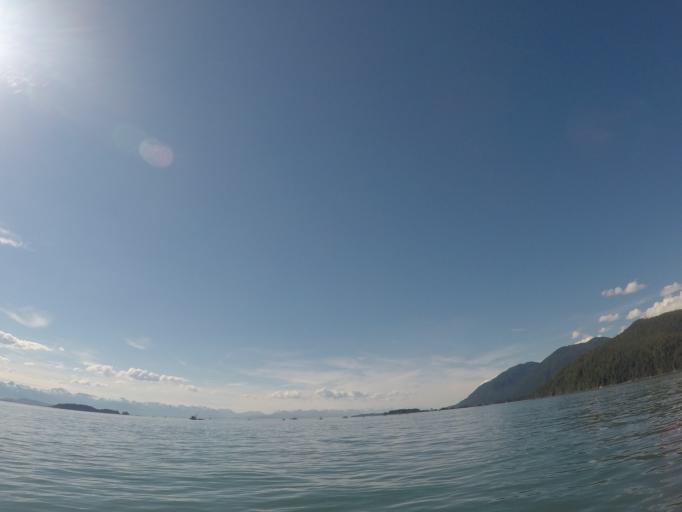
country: US
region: Alaska
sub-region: Juneau City and Borough
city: Juneau
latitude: 58.4937
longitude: -134.8142
